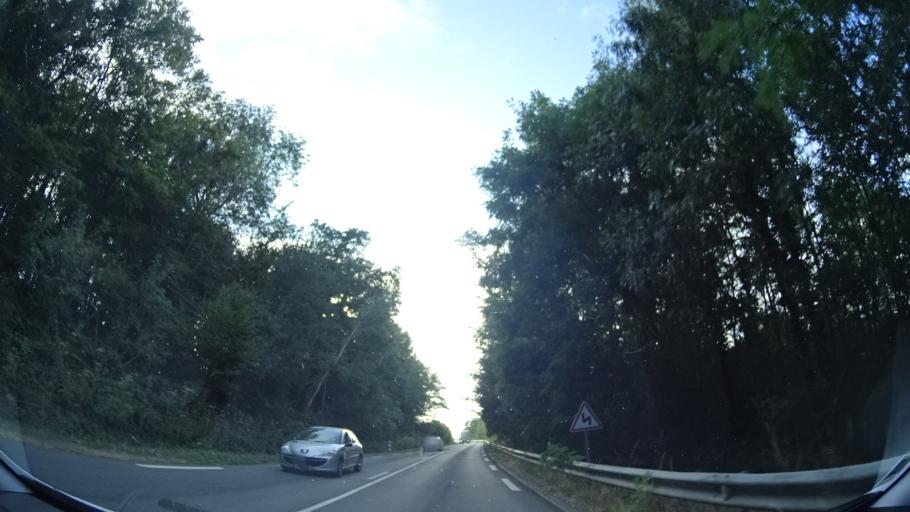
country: FR
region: Centre
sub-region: Departement du Loir-et-Cher
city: Moree
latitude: 47.8943
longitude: 1.1693
